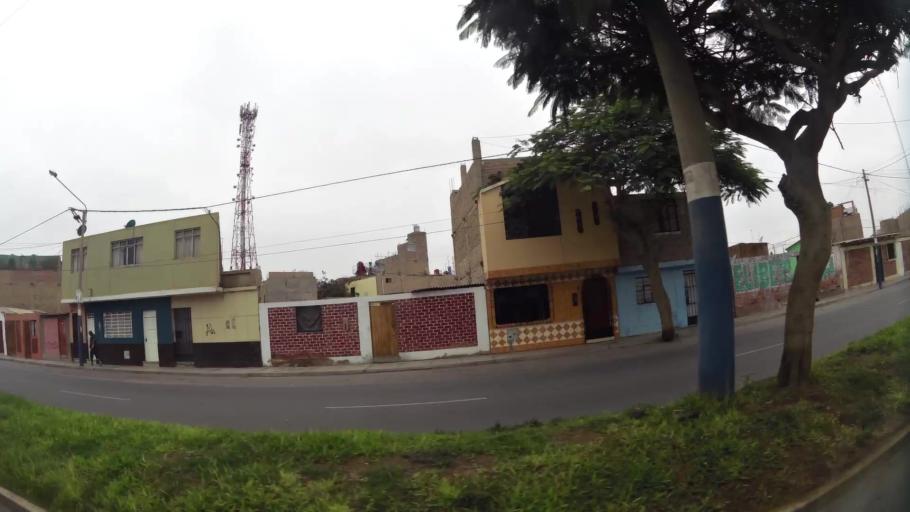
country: PE
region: Ica
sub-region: Provincia de Pisco
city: Pisco
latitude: -13.7088
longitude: -76.2061
